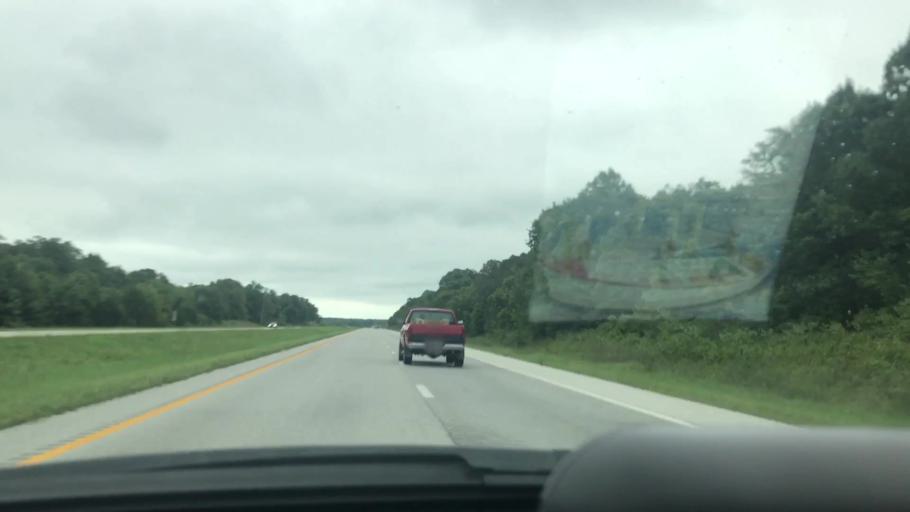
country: US
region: Missouri
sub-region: Greene County
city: Strafford
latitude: 37.2825
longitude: -93.2000
